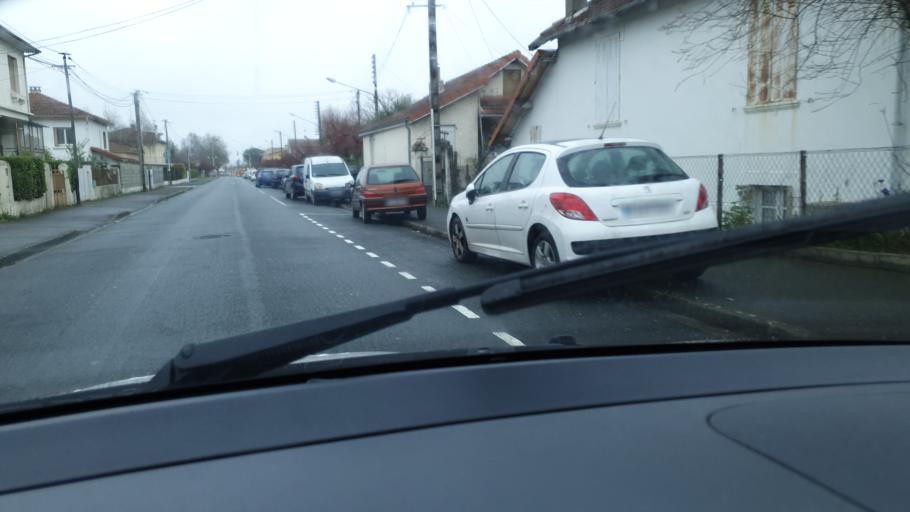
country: FR
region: Midi-Pyrenees
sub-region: Departement des Hautes-Pyrenees
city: Tarbes
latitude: 43.2380
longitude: 0.0515
